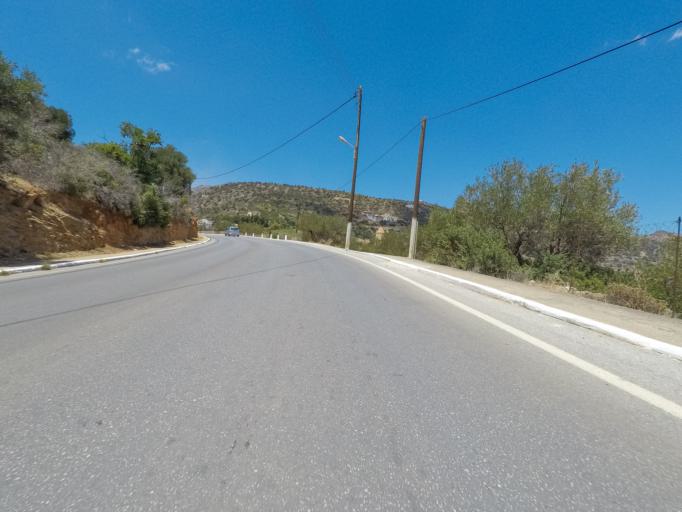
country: GR
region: Crete
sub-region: Nomos Lasithiou
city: Agios Nikolaos
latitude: 35.2161
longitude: 25.7124
